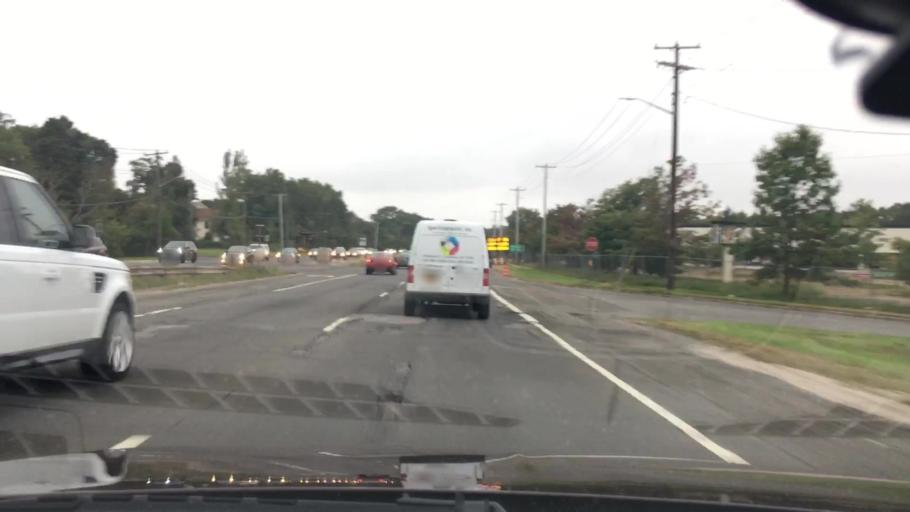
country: US
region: New York
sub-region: Suffolk County
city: Nesconset
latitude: 40.8605
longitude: -73.1398
